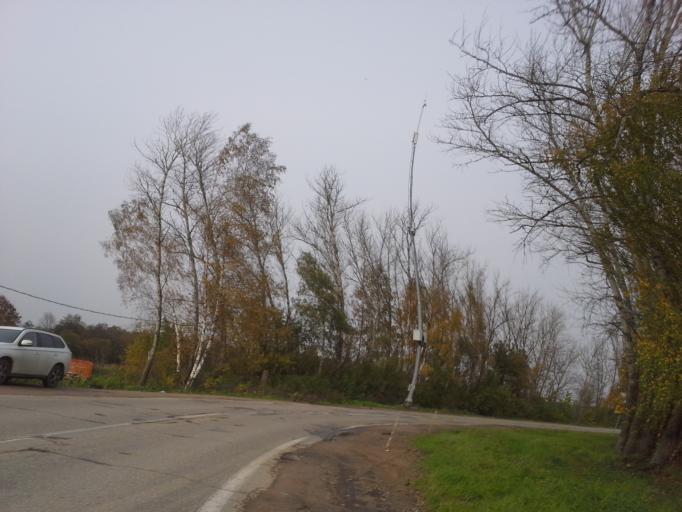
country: RU
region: Moskovskaya
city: Bol'shiye Vyazemy
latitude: 55.6390
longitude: 36.9991
